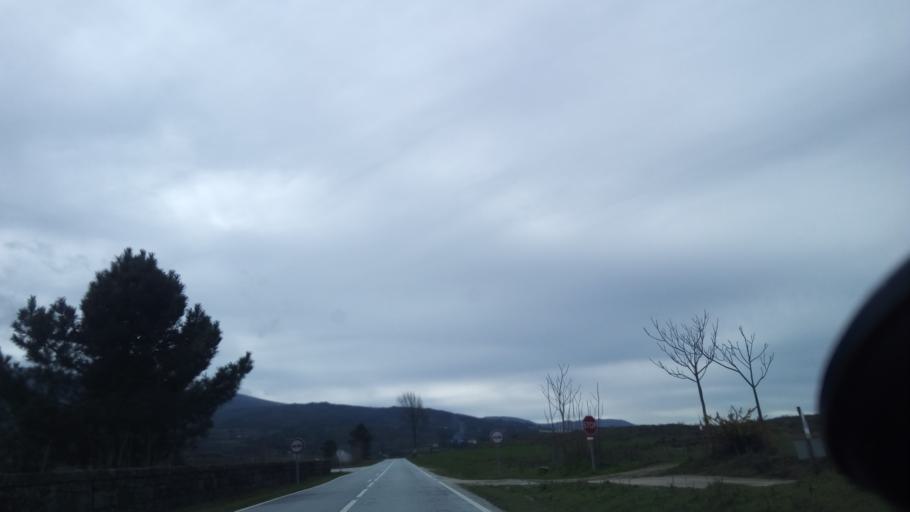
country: PT
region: Guarda
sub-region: Fornos de Algodres
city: Fornos de Algodres
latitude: 40.5394
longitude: -7.5698
